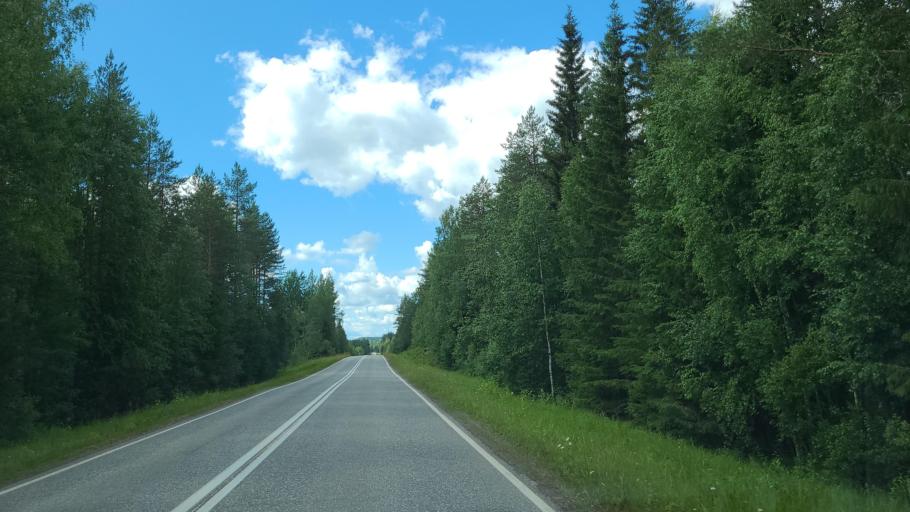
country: FI
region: Northern Savo
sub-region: Koillis-Savo
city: Kaavi
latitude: 62.9835
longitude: 28.8092
